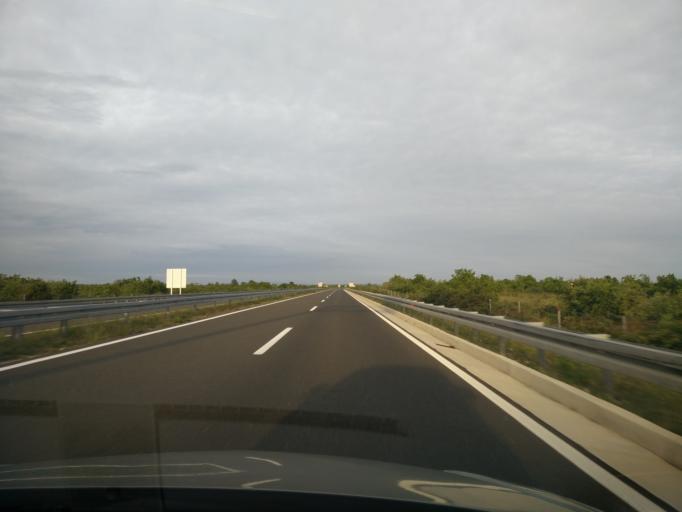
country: HR
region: Zadarska
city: Galovac
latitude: 44.1190
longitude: 15.4240
